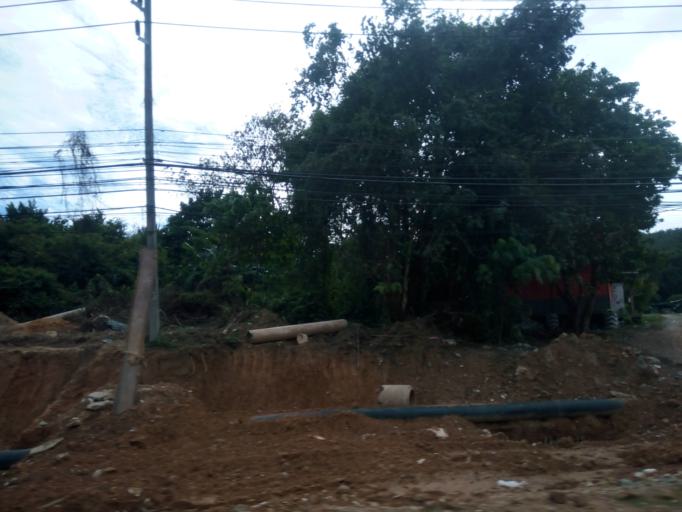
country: TH
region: Phuket
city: Mueang Phuket
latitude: 7.8348
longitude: 98.3954
